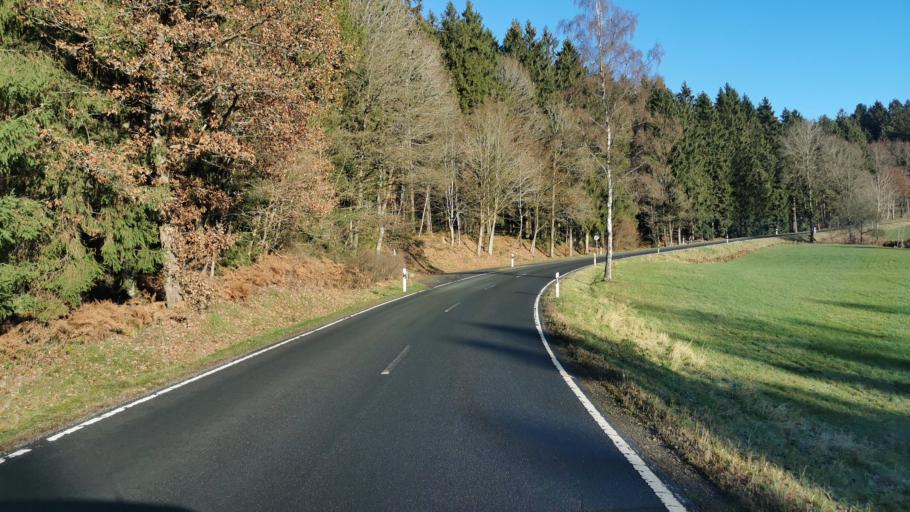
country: DE
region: Rheinland-Pfalz
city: Meisburg
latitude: 50.1129
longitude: 6.6823
